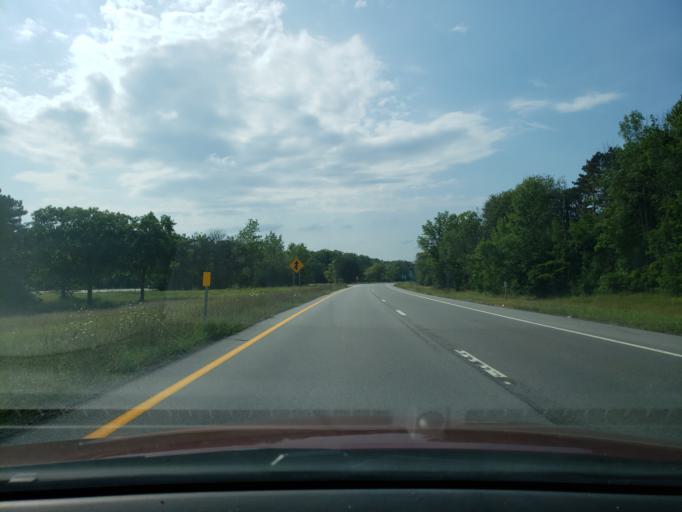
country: US
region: New York
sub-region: Monroe County
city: Irondequoit
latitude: 43.2567
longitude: -77.6337
